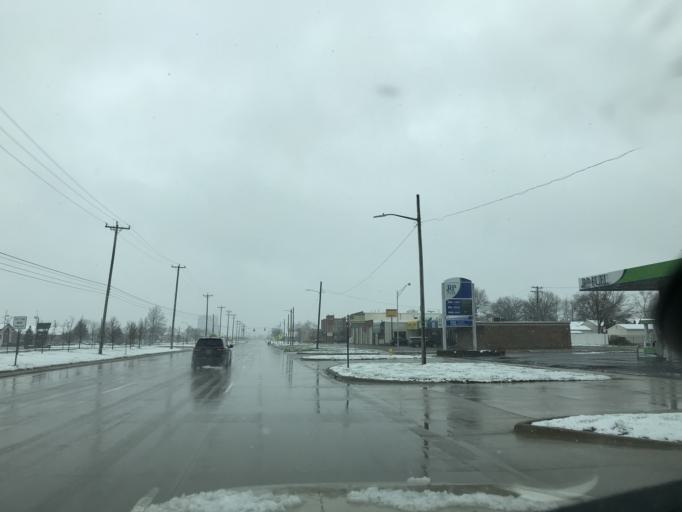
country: US
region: Michigan
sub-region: Wayne County
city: Riverview
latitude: 42.1752
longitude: -83.1889
